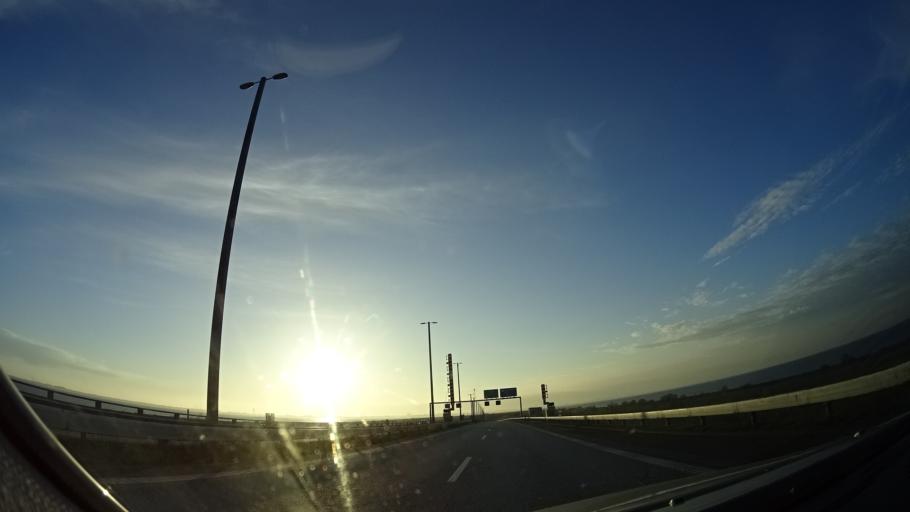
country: DK
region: Capital Region
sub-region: Dragor Kommune
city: Dragor
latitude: 55.6072
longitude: 12.7361
